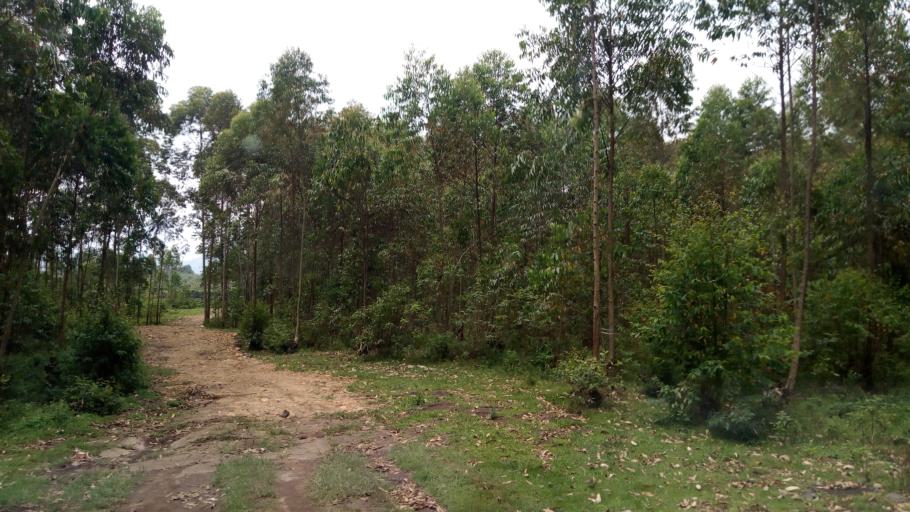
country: UG
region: Western Region
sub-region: Kisoro District
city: Kisoro
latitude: -1.2648
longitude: 29.6036
